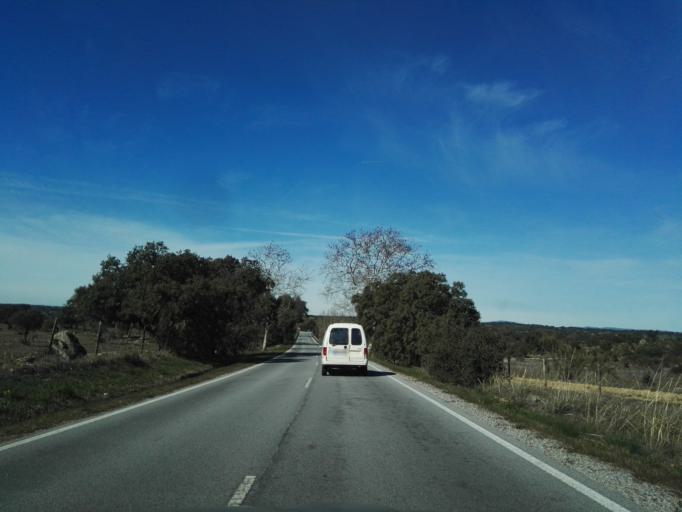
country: PT
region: Portalegre
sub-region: Arronches
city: Arronches
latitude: 39.0494
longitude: -7.2655
